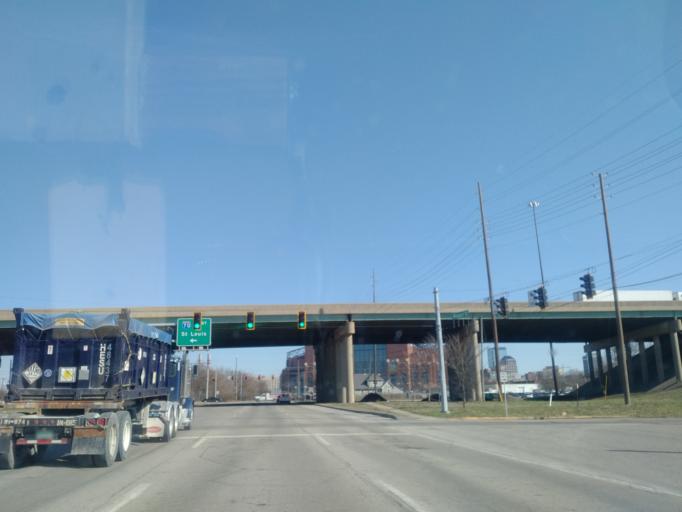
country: US
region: Indiana
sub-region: Marion County
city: Indianapolis
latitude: 39.7528
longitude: -86.1662
